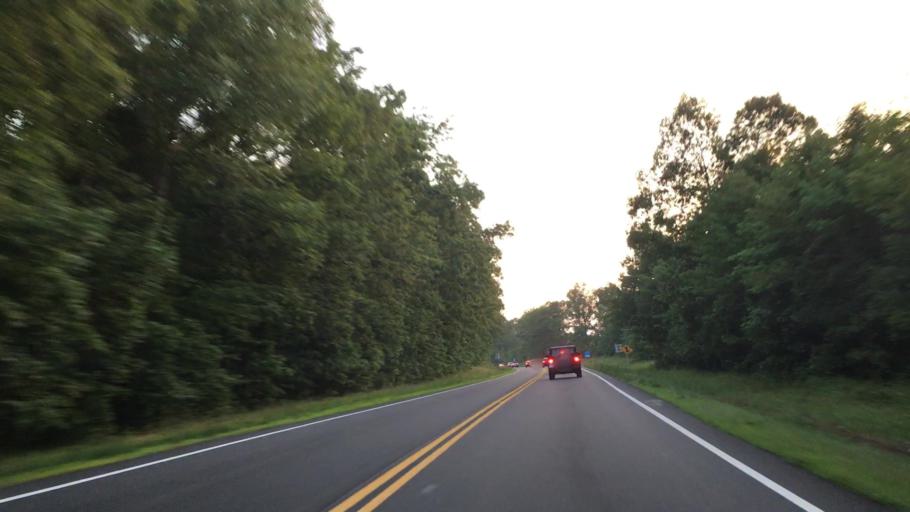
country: US
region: Virginia
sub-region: Culpeper County
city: Culpeper
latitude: 38.2876
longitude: -77.8644
